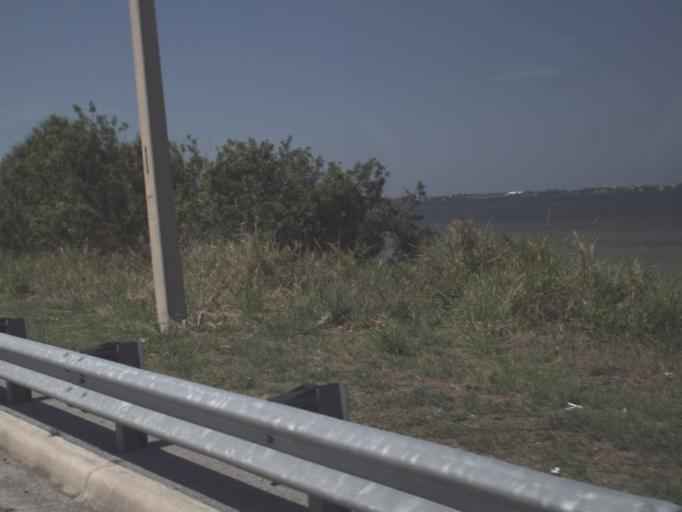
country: US
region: Florida
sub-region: Brevard County
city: Melbourne
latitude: 28.1082
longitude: -80.6172
